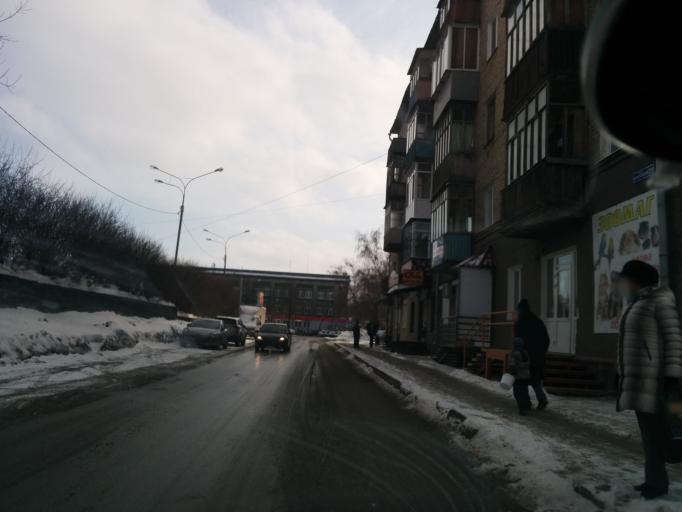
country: RU
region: Perm
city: Perm
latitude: 58.0204
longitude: 56.2748
